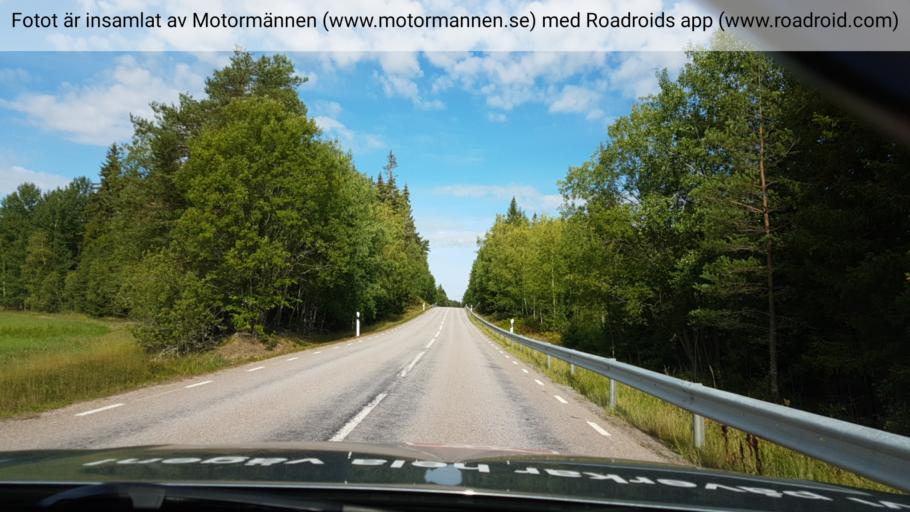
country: SE
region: Uppsala
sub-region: Heby Kommun
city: OEstervala
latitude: 59.9932
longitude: 17.3186
